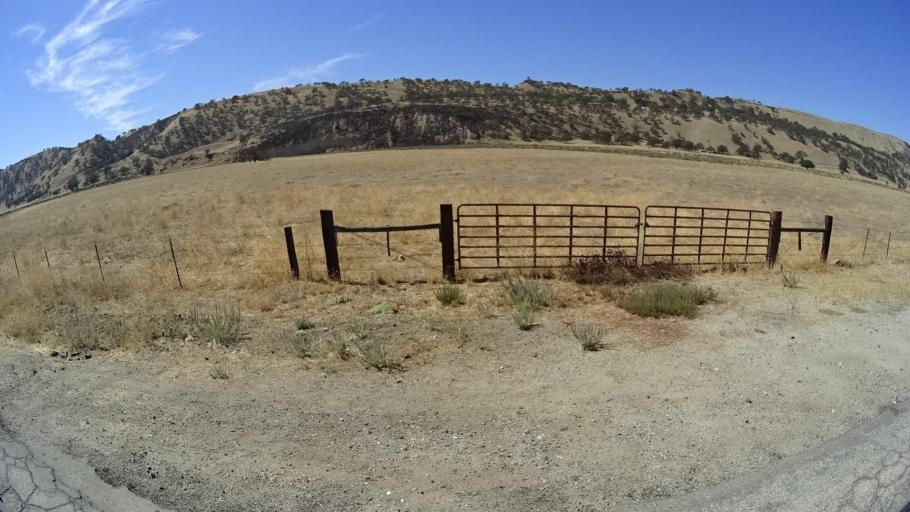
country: US
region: California
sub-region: San Luis Obispo County
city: San Miguel
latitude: 35.8624
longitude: -120.7011
